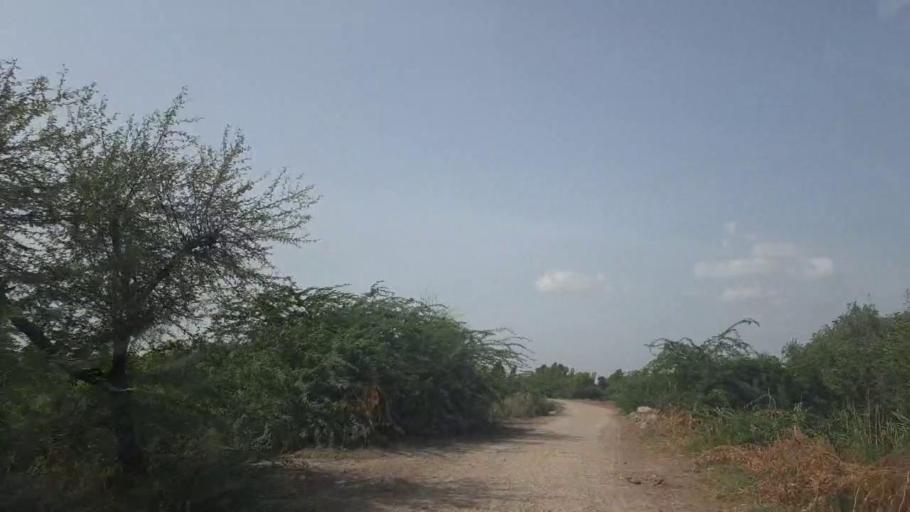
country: PK
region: Sindh
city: Tando Bago
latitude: 24.7803
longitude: 69.1300
